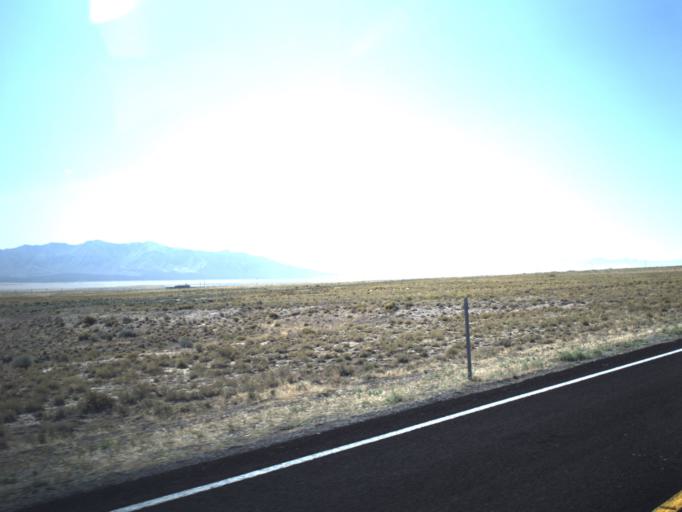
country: US
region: Utah
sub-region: Beaver County
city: Milford
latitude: 38.4751
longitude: -112.9920
